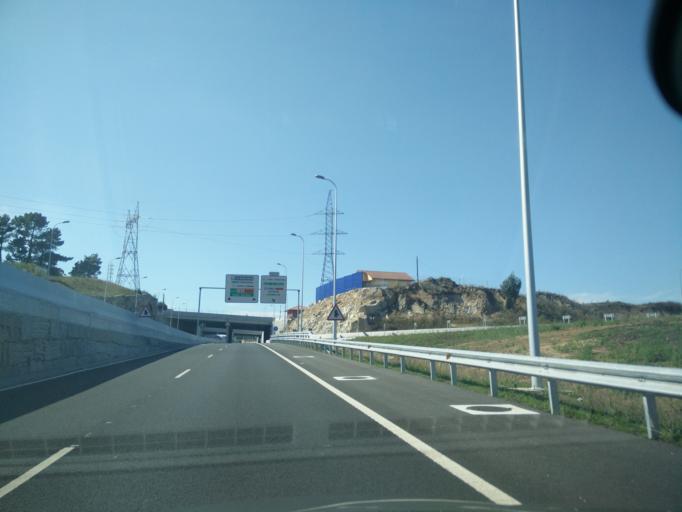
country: ES
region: Galicia
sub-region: Provincia da Coruna
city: A Coruna
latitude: 43.3385
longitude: -8.4235
